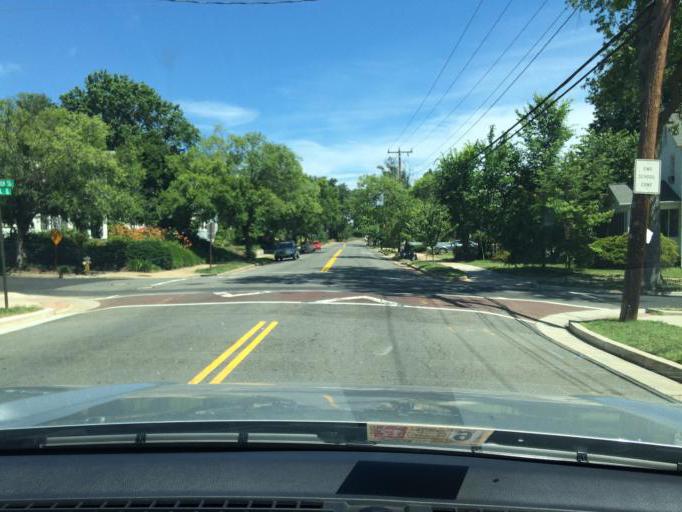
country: US
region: Virginia
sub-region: City of Alexandria
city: Alexandria
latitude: 38.8138
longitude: -77.0650
